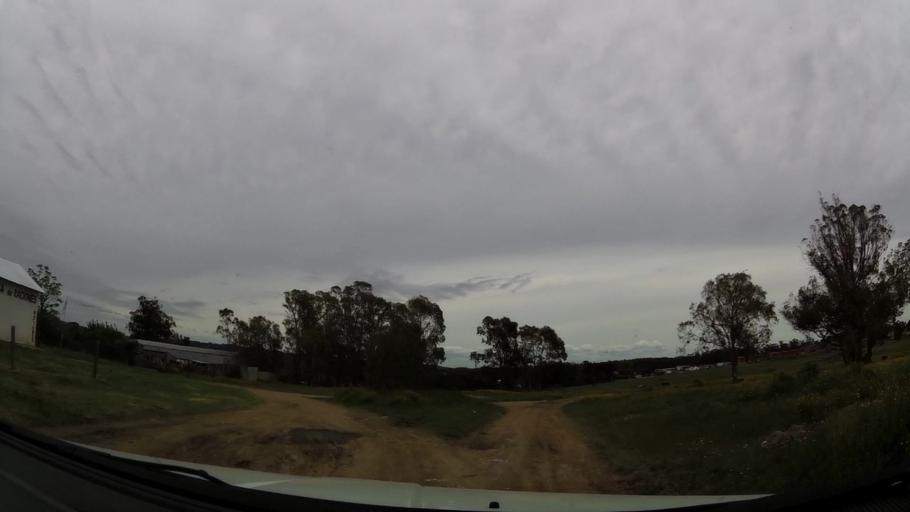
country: UY
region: Maldonado
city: Maldonado
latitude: -34.8801
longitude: -54.9841
